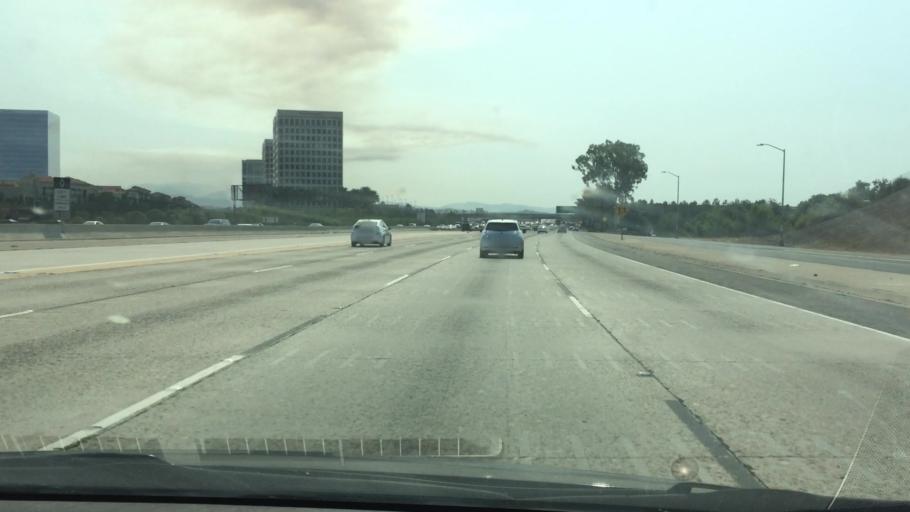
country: US
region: California
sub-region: Orange County
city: Laguna Woods
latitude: 33.6510
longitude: -117.7579
